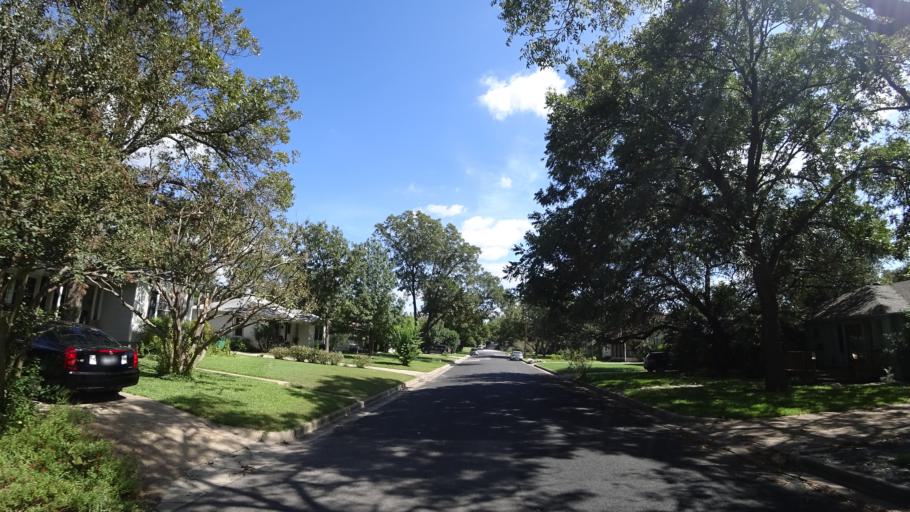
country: US
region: Texas
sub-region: Travis County
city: Austin
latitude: 30.3457
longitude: -97.7262
